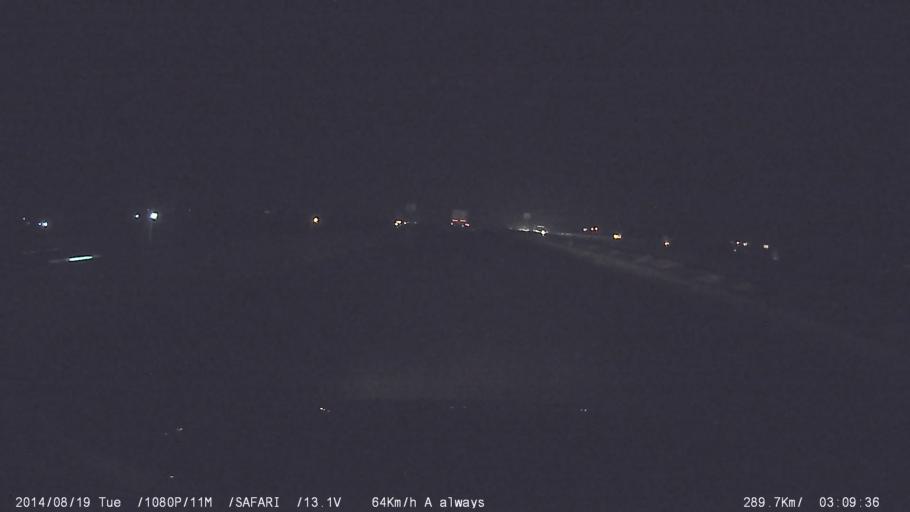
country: IN
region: Tamil Nadu
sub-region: Coimbatore
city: Sulur
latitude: 11.0928
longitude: 77.1441
